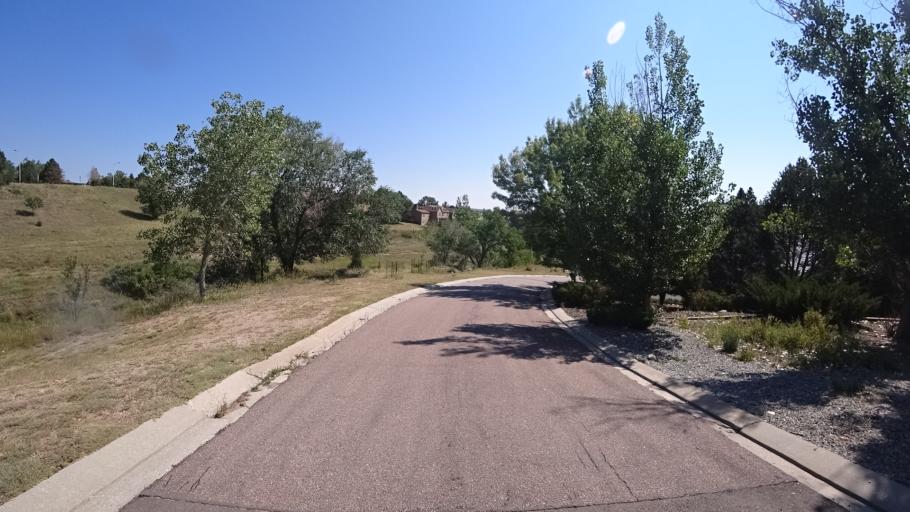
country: US
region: Colorado
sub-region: El Paso County
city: Air Force Academy
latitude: 38.9282
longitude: -104.8228
